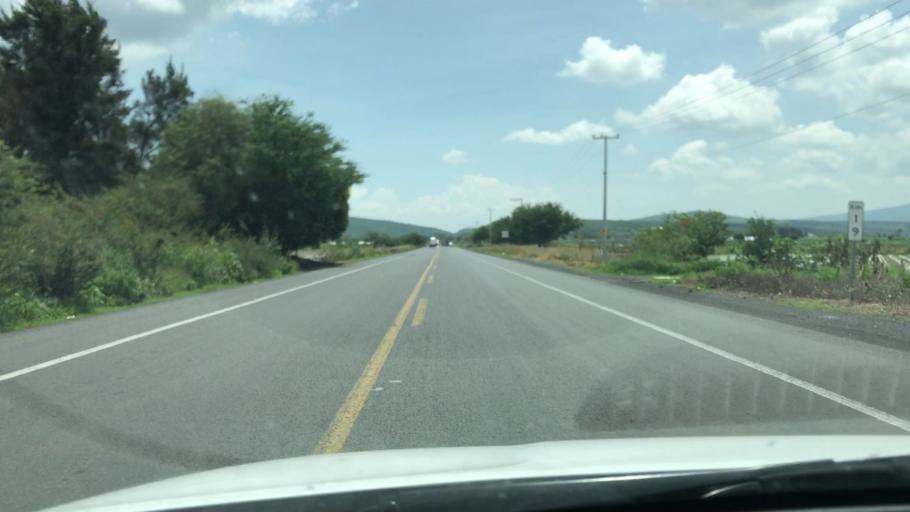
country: MX
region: Michoacan
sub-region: Yurecuaro
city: Yurecuaro
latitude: 20.3254
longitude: -102.2755
